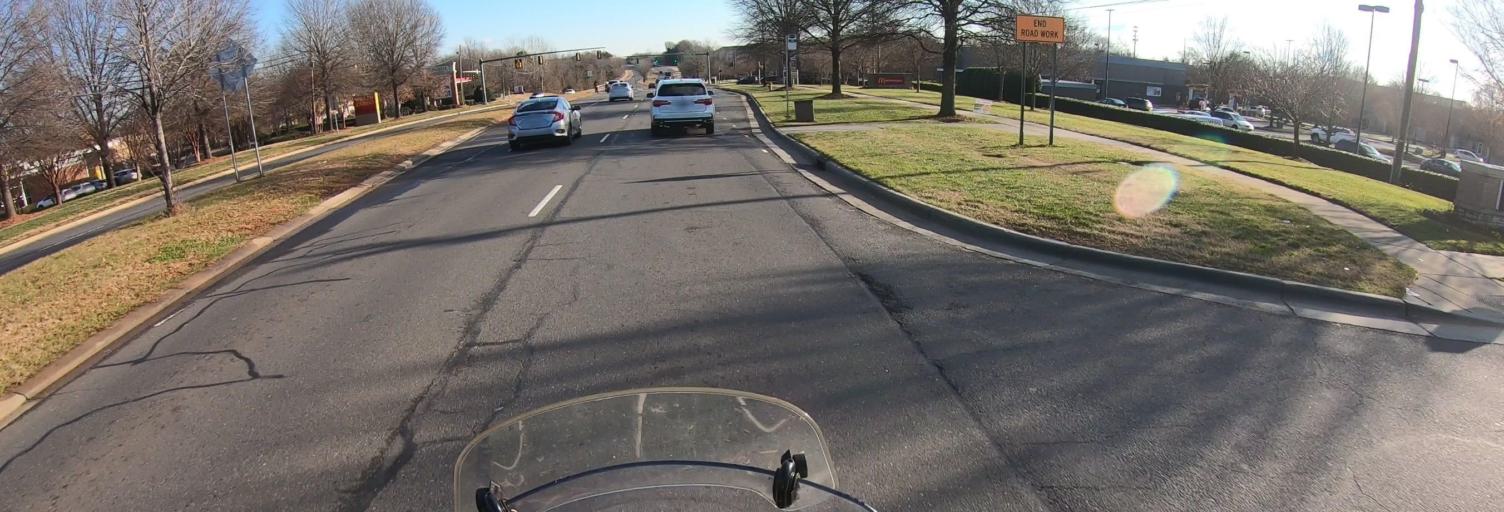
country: US
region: South Carolina
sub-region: York County
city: Lake Wylie
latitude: 35.1035
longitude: -80.9870
